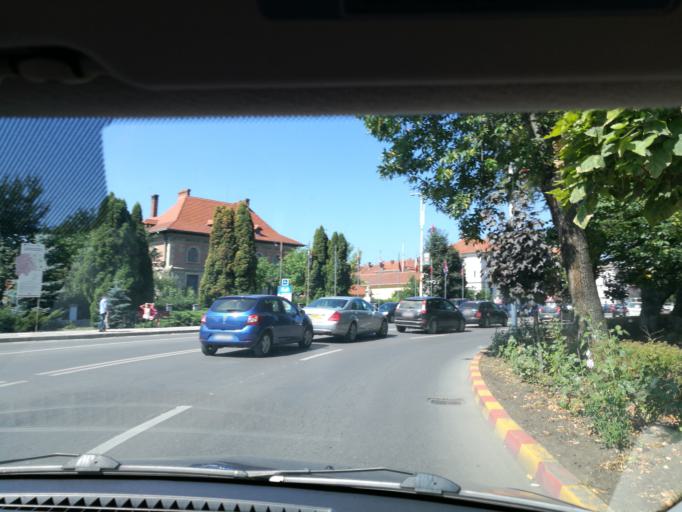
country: RO
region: Suceava
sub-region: Municipiul Suceava
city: Radauti
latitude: 47.8434
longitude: 25.9177
